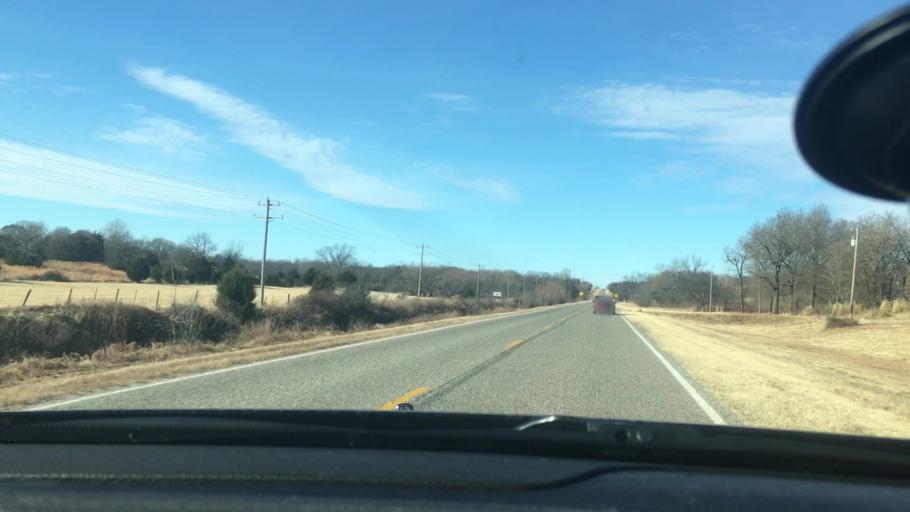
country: US
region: Oklahoma
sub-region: Cleveland County
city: Lexington
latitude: 35.0149
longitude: -97.1536
